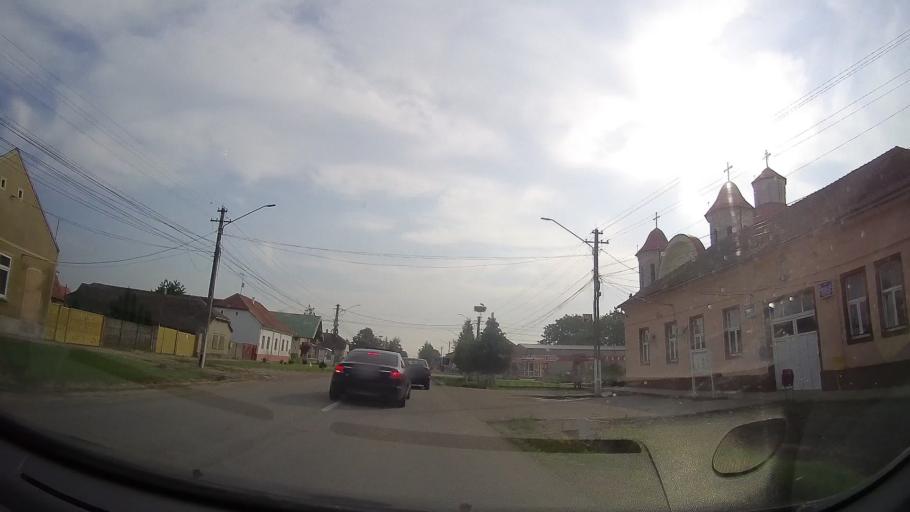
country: RO
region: Timis
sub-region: Comuna Peciu Nou
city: Peciu Nou
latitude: 45.6058
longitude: 21.0578
